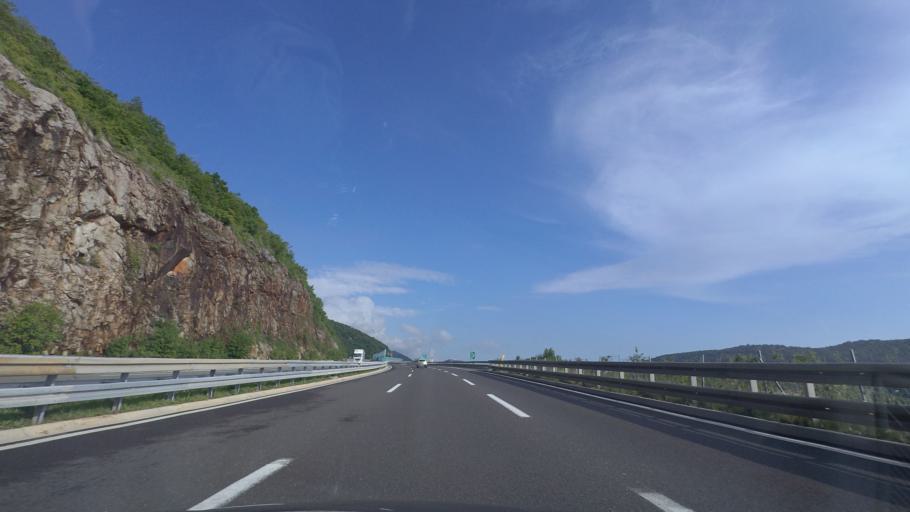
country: HR
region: Primorsko-Goranska
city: Skrljevo
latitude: 45.3691
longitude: 14.5464
